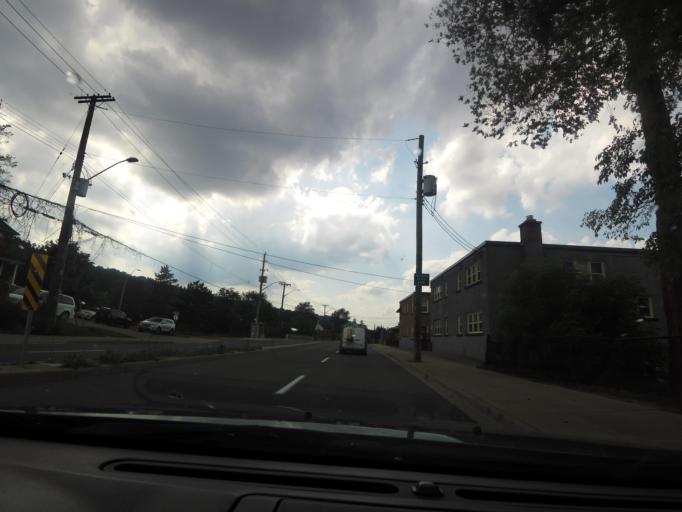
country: CA
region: Ontario
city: Hamilton
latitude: 43.2326
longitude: -79.8120
